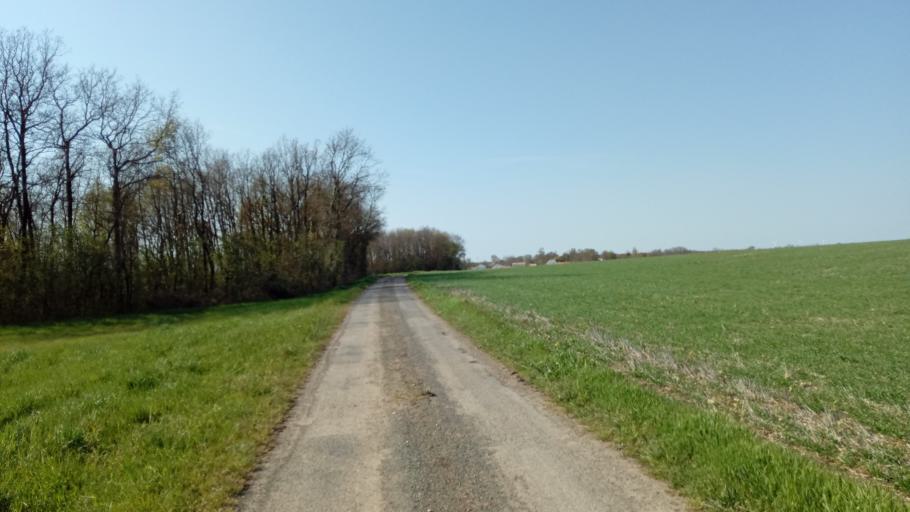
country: FR
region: Poitou-Charentes
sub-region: Departement de la Charente-Maritime
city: Verines
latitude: 46.1618
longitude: -0.9388
